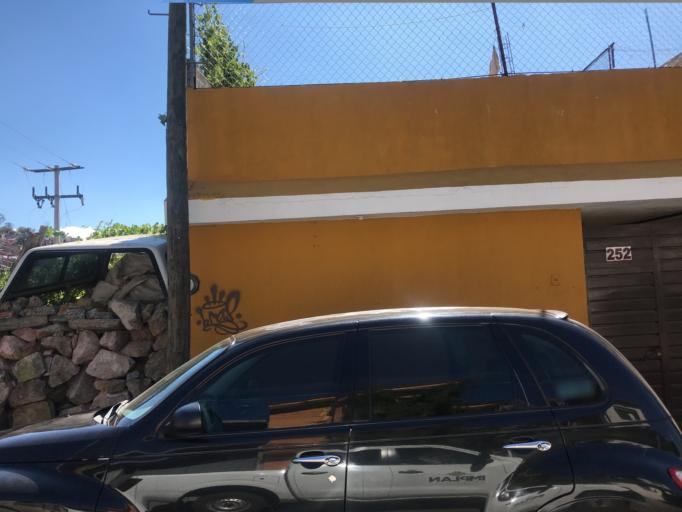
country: MX
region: Michoacan
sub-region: Morelia
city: Puerto de Buenavista (Lazaro Cardenas)
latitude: 19.7022
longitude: -101.1448
